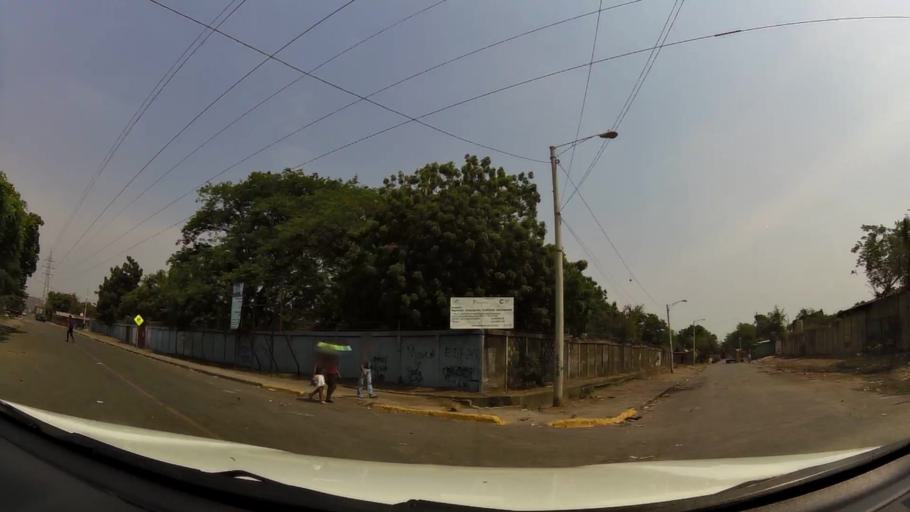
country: NI
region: Managua
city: Ciudad Sandino
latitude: 12.1608
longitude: -86.2969
